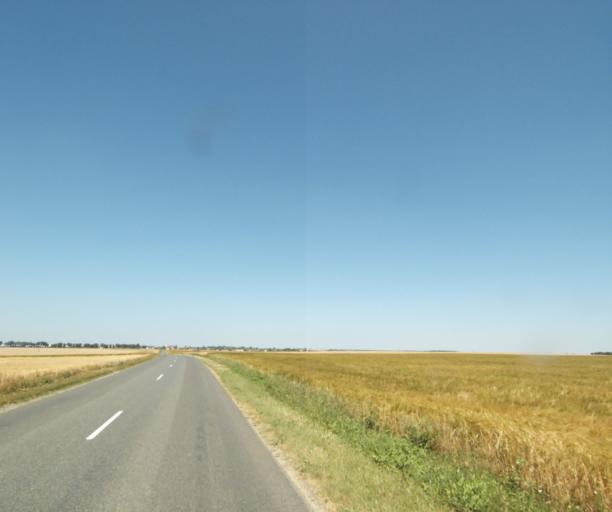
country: FR
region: Ile-de-France
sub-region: Departement de Seine-et-Marne
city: La Chapelle-la-Reine
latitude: 48.3019
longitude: 2.5548
